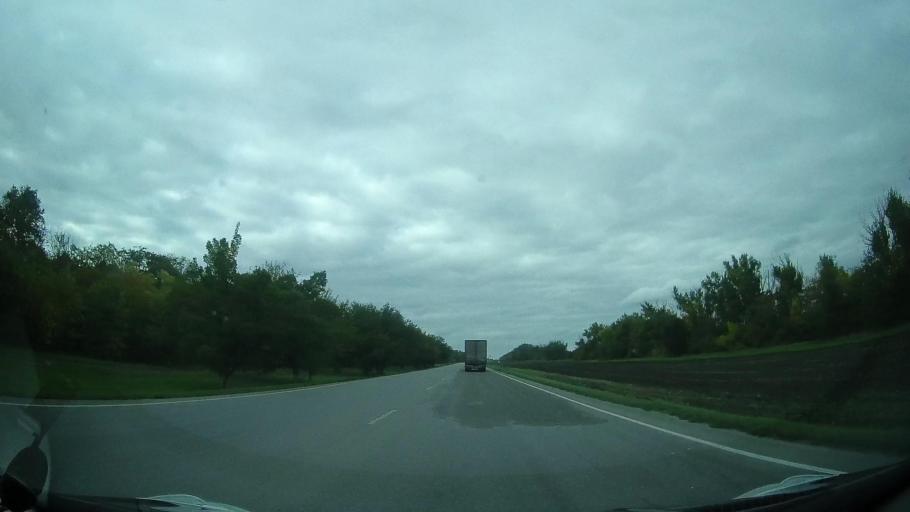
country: RU
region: Rostov
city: Yegorlykskaya
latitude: 46.6217
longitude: 40.5964
